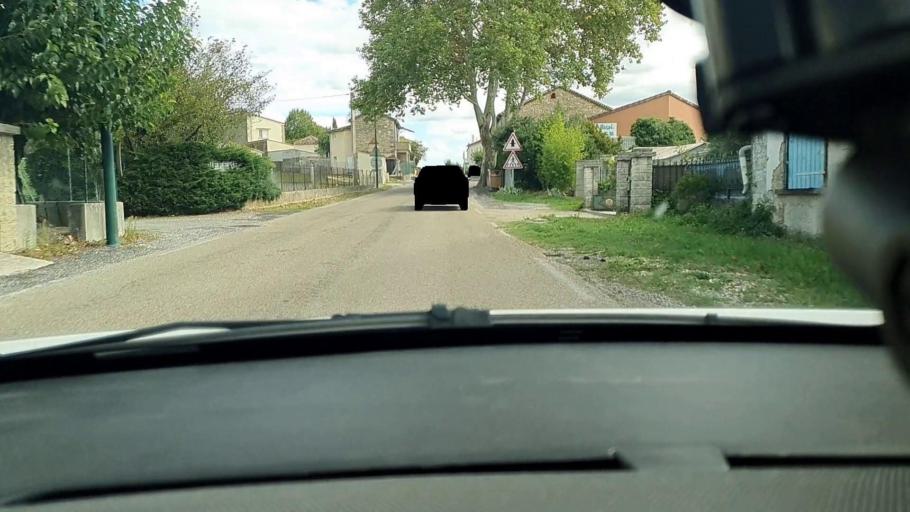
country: FR
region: Languedoc-Roussillon
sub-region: Departement du Gard
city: Les Mages
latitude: 44.2122
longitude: 4.1960
